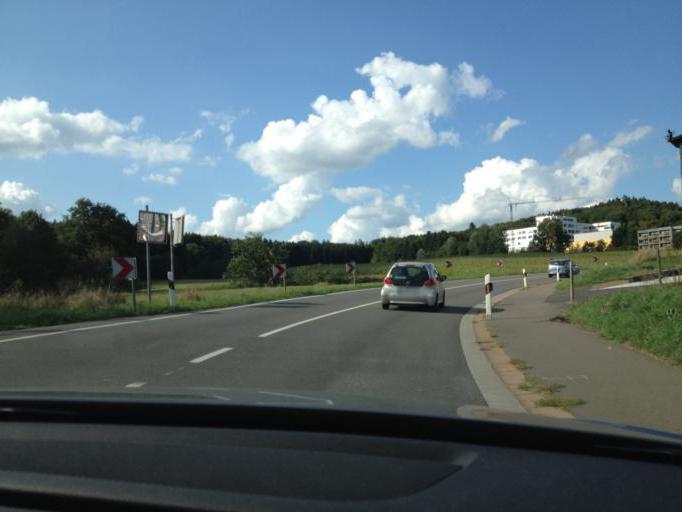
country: DE
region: Saarland
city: Lebach
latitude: 49.4154
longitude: 6.8915
